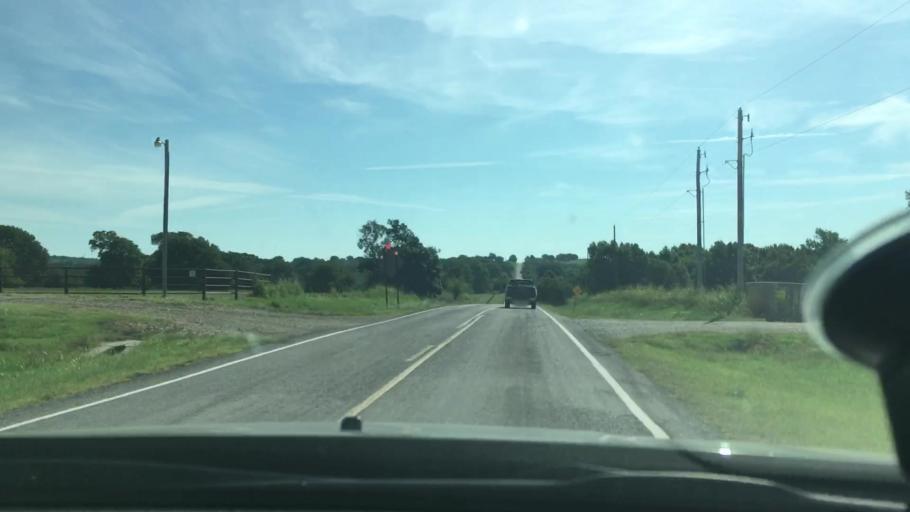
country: US
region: Oklahoma
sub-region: Carter County
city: Lone Grove
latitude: 34.3327
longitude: -97.2392
